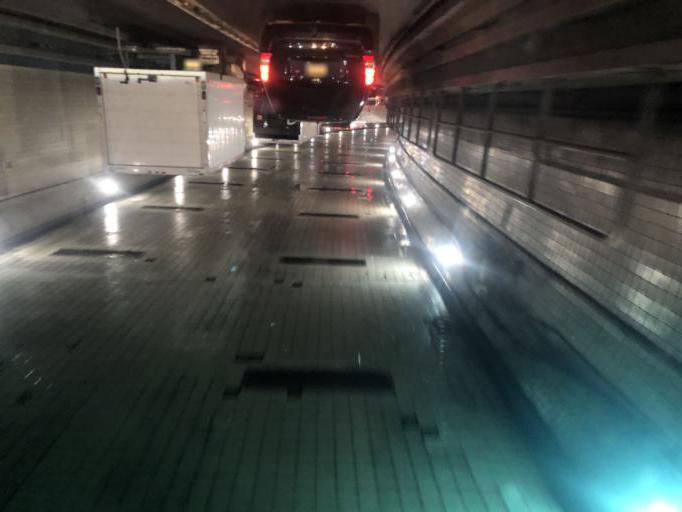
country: US
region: New Jersey
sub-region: Hudson County
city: Hoboken
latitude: 40.7564
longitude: -74.0293
